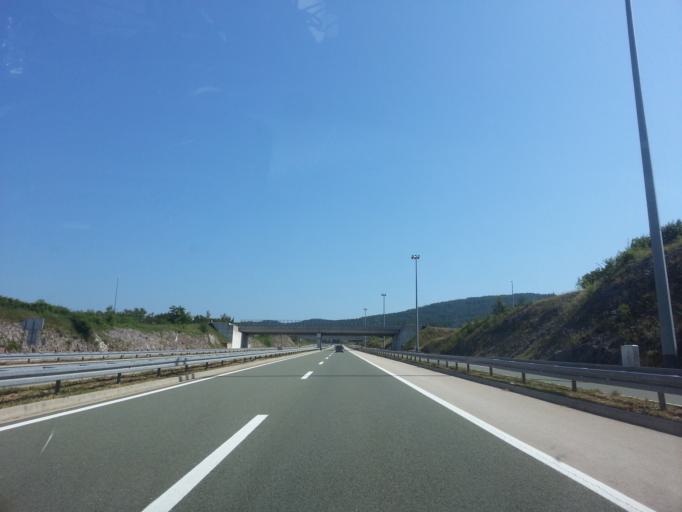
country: HR
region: Primorsko-Goranska
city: Klana
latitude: 45.4722
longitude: 14.2749
